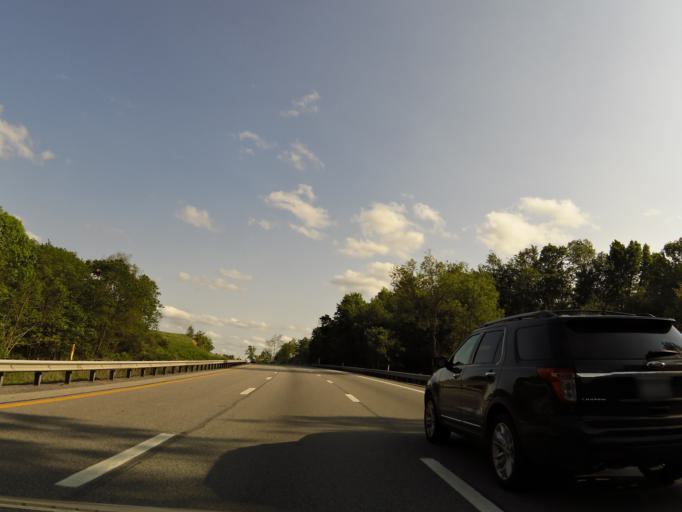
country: US
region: West Virginia
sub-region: Mercer County
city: Princeton
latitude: 37.4004
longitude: -81.0638
